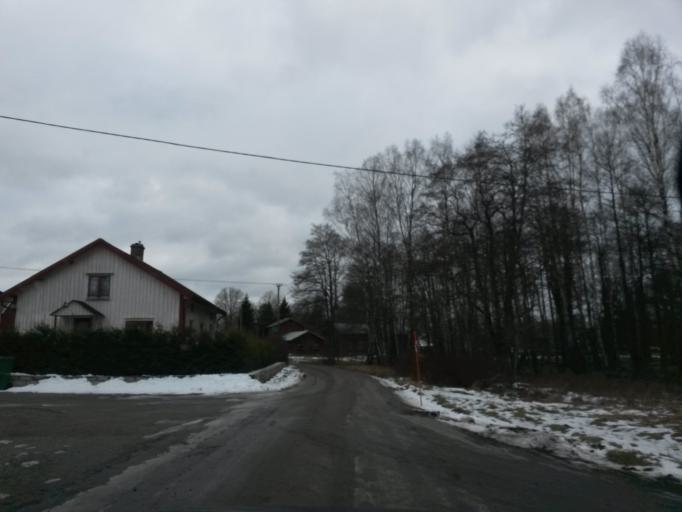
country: SE
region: Vaestra Goetaland
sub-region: Vargarda Kommun
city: Vargarda
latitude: 58.0320
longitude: 12.8904
